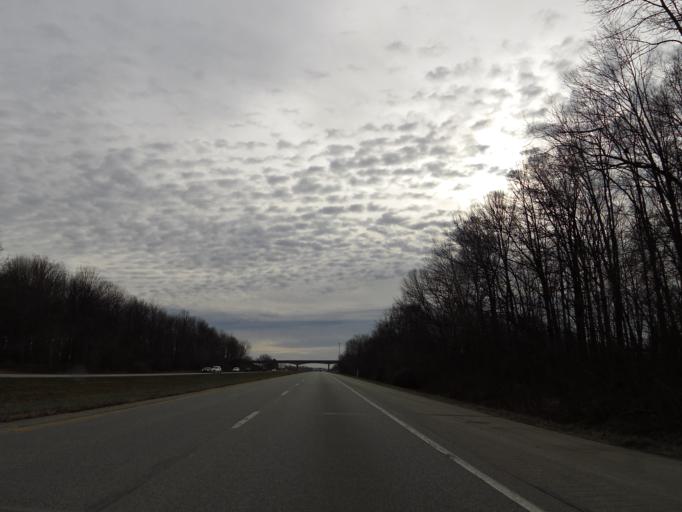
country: US
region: Indiana
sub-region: Hendricks County
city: Pittsboro
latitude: 39.9252
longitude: -86.5874
